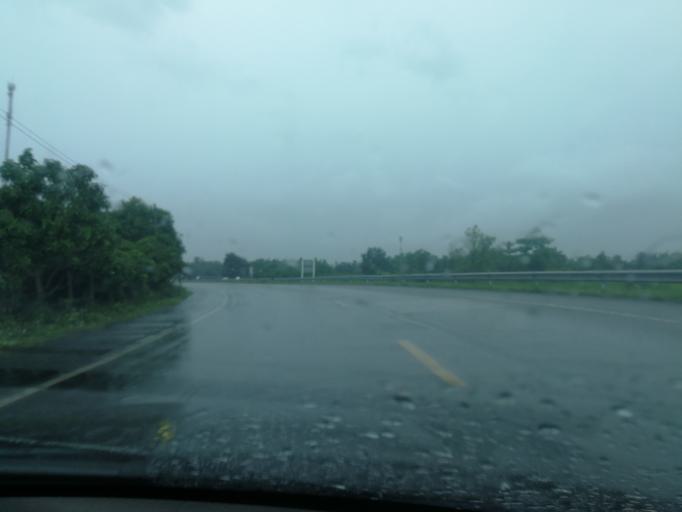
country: TH
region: Chiang Mai
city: San Pa Tong
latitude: 18.6402
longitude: 98.8461
